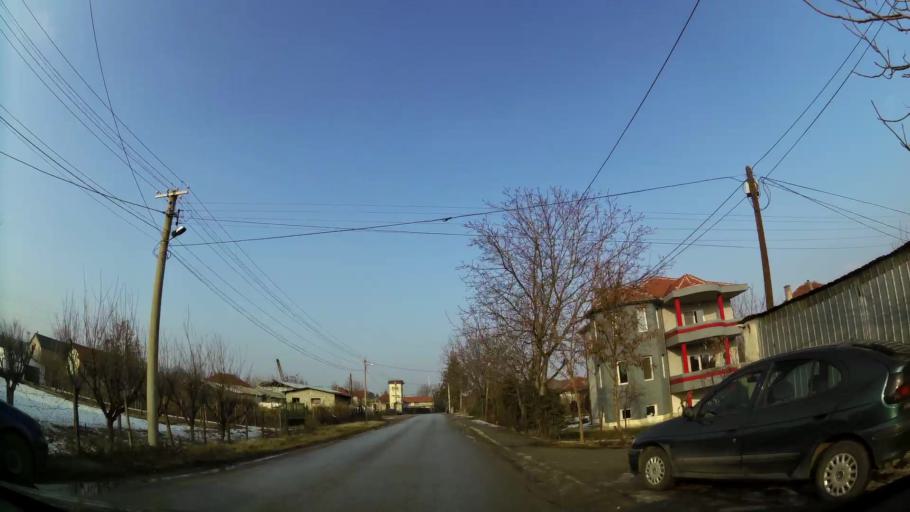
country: MK
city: Miladinovci
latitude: 41.9858
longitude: 21.6513
